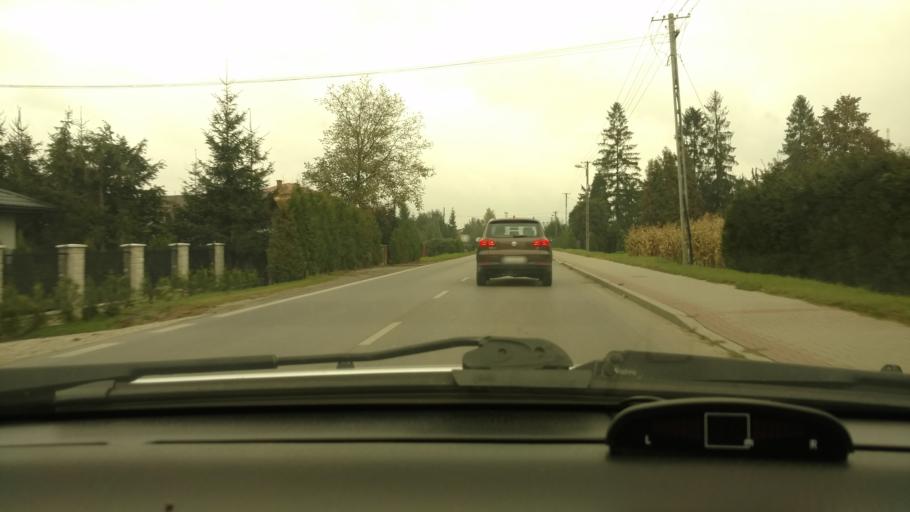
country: PL
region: Lesser Poland Voivodeship
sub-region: Powiat nowosadecki
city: Chelmiec
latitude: 49.6188
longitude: 20.6663
